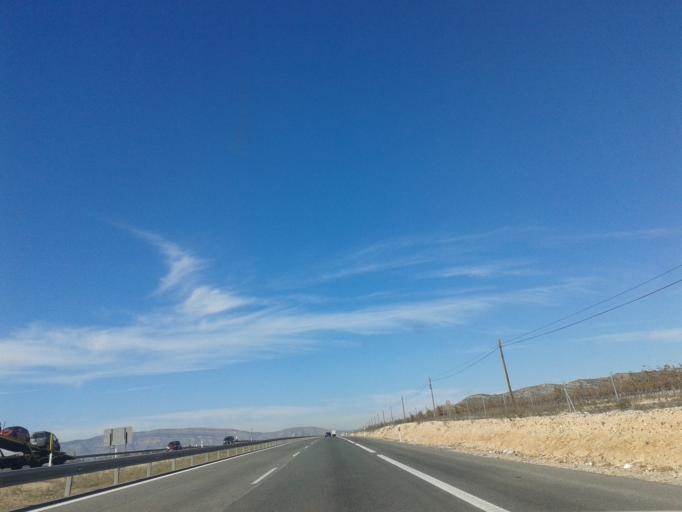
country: ES
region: Valencia
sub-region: Provincia de Alicante
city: Villena
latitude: 38.6792
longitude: -0.8964
